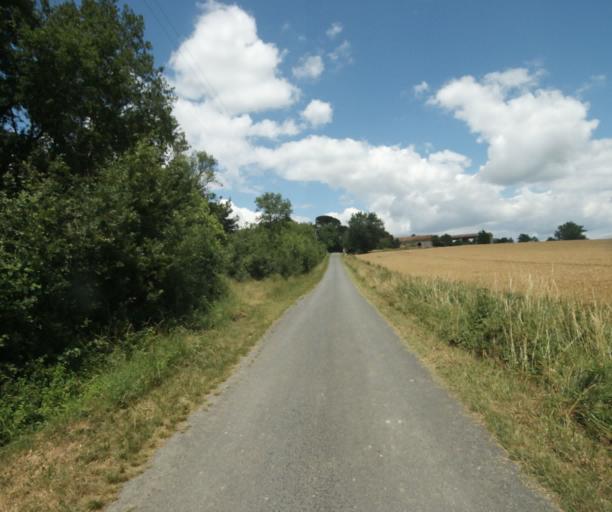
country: FR
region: Midi-Pyrenees
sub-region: Departement du Tarn
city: Puylaurens
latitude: 43.5229
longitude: 2.0240
